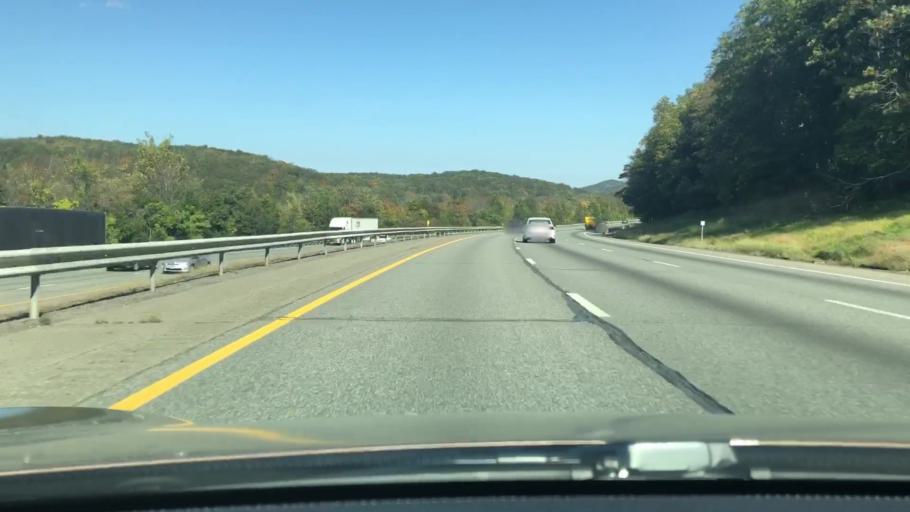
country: US
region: New York
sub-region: Rockland County
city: Sloatsburg
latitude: 41.1712
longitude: -74.1864
